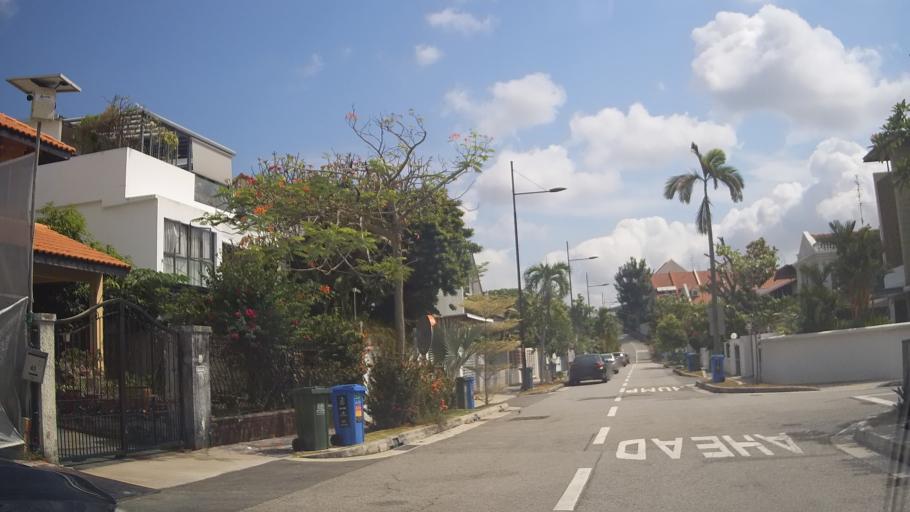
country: SG
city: Singapore
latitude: 1.3240
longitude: 103.9479
